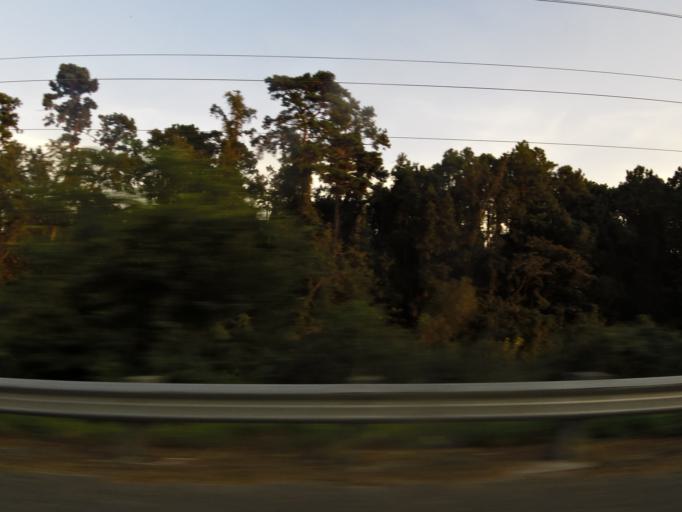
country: US
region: Florida
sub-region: Leon County
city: Tallahassee
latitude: 30.4838
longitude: -84.3032
